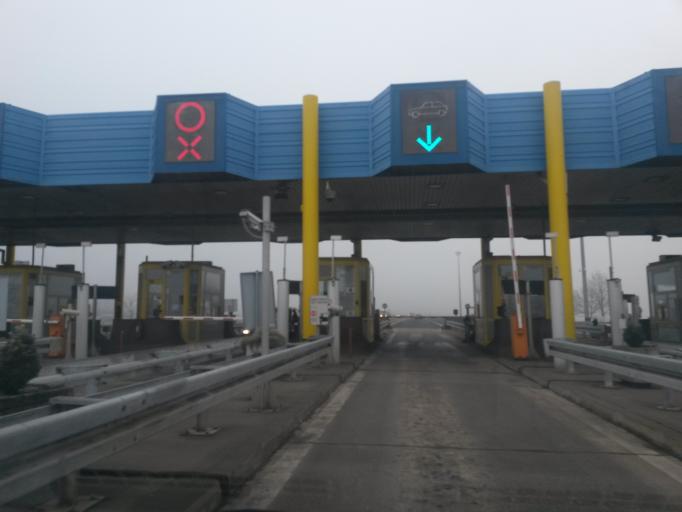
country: HR
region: Zagrebacka
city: Brckovljani
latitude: 45.9203
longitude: 16.2737
